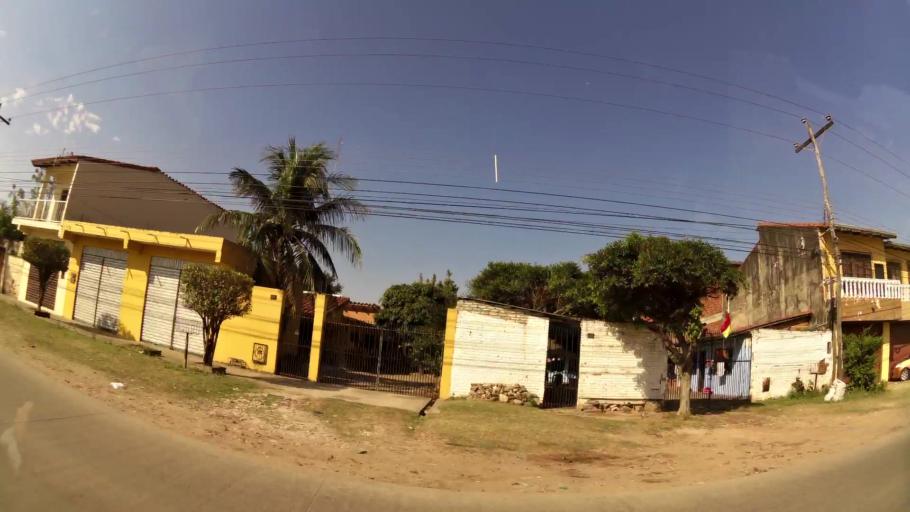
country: BO
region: Santa Cruz
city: Santa Cruz de la Sierra
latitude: -17.7992
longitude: -63.1422
